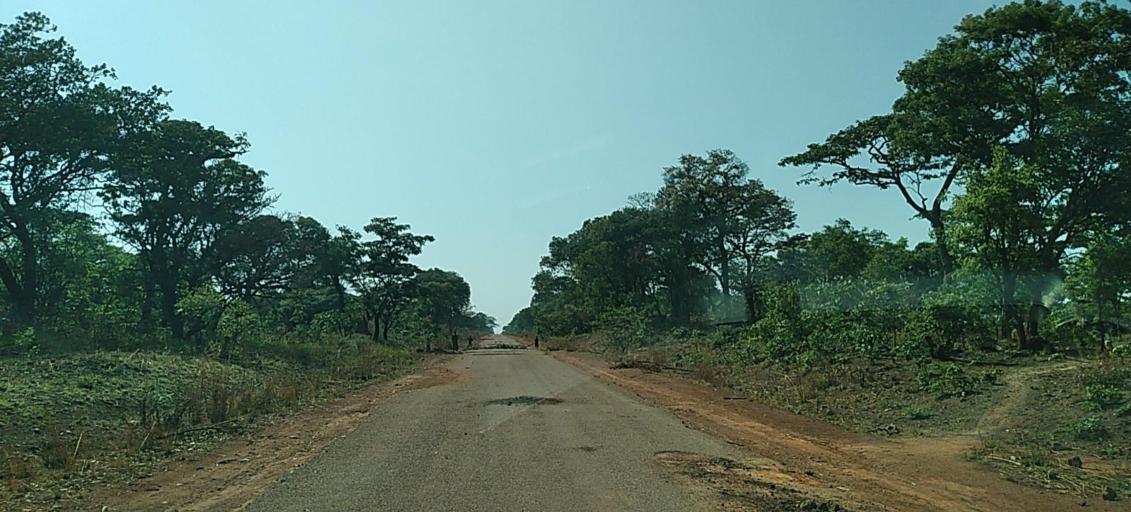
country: ZM
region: North-Western
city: Mwinilunga
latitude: -11.9052
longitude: 25.2873
